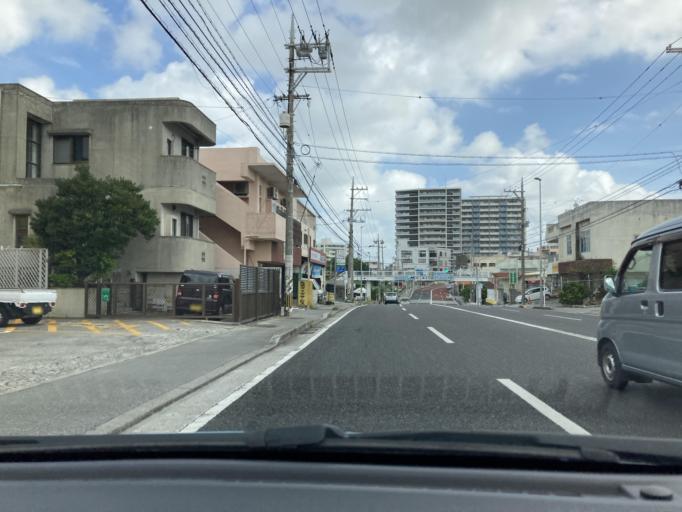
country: JP
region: Okinawa
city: Ginowan
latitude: 26.2573
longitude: 127.7410
